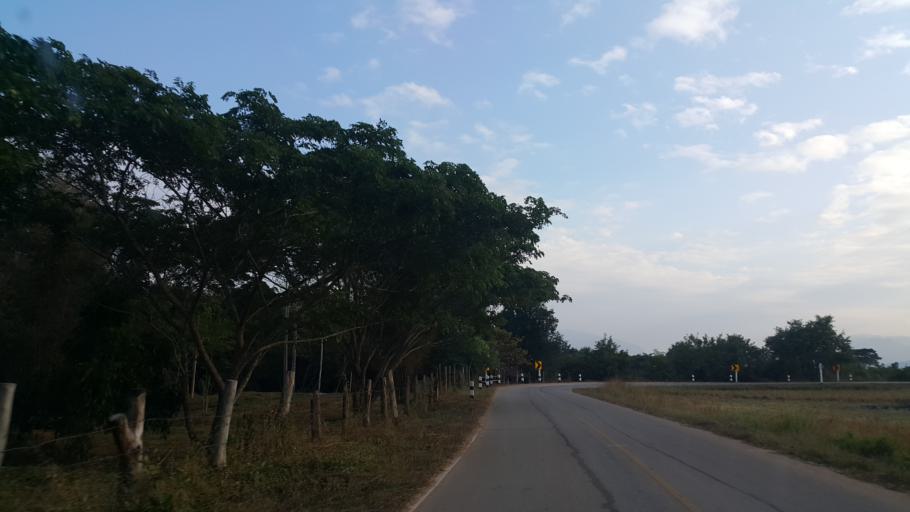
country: TH
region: Lampang
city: Sop Prap
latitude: 17.9192
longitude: 99.3279
